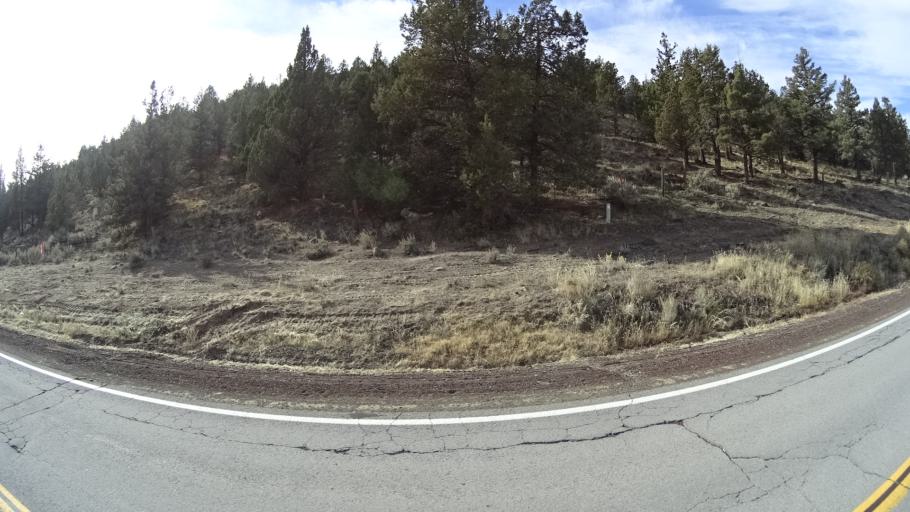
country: US
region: California
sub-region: Siskiyou County
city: Weed
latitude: 41.5403
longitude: -122.3656
